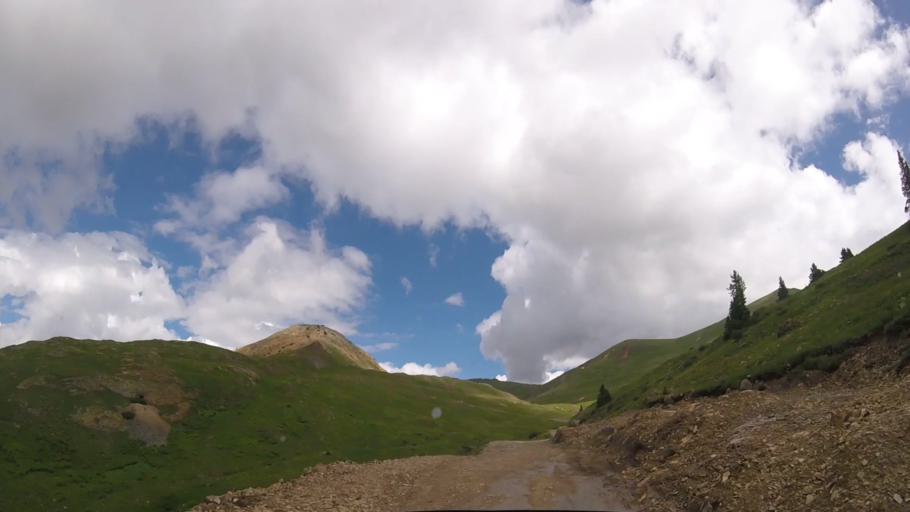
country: US
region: Colorado
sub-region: Ouray County
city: Ouray
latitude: 37.9459
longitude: -107.5741
